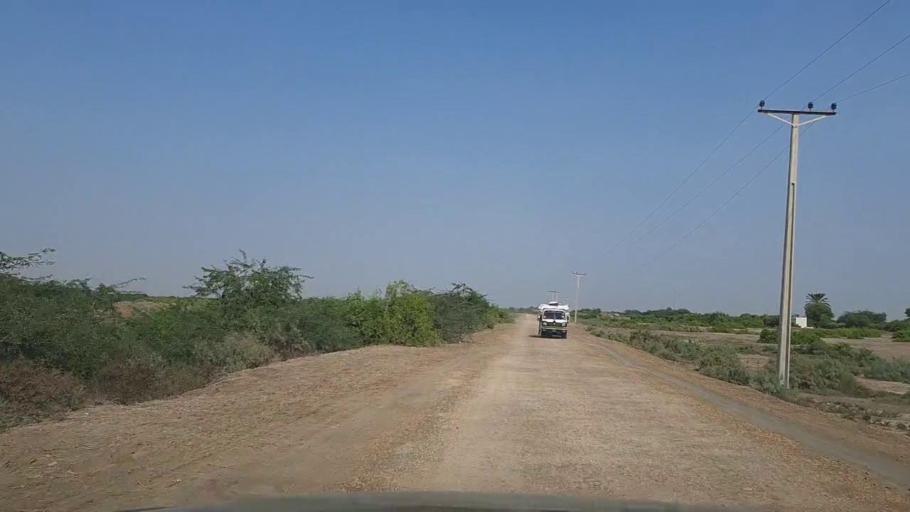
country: PK
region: Sindh
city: Thatta
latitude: 24.6045
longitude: 67.9540
